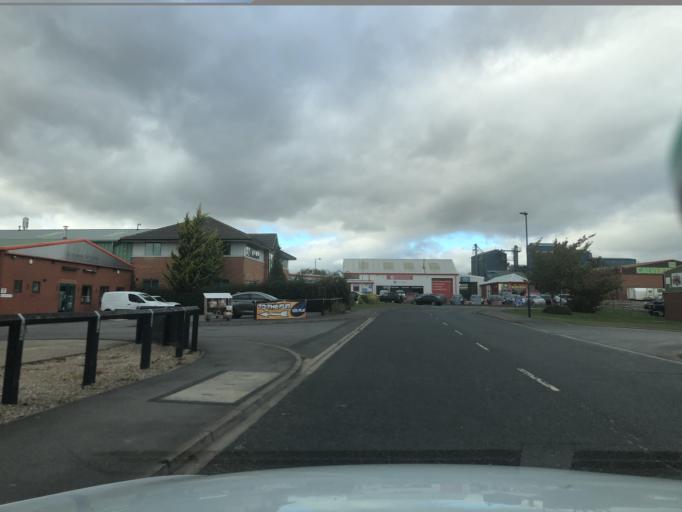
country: GB
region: England
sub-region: North Yorkshire
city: Northallerton
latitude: 54.3492
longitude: -1.4492
